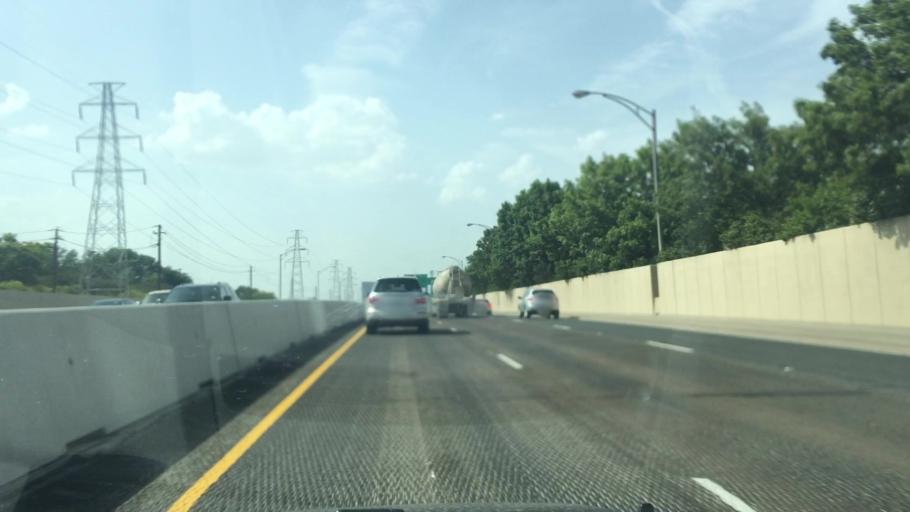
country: US
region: Texas
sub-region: Dallas County
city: University Park
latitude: 32.9033
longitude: -96.8144
